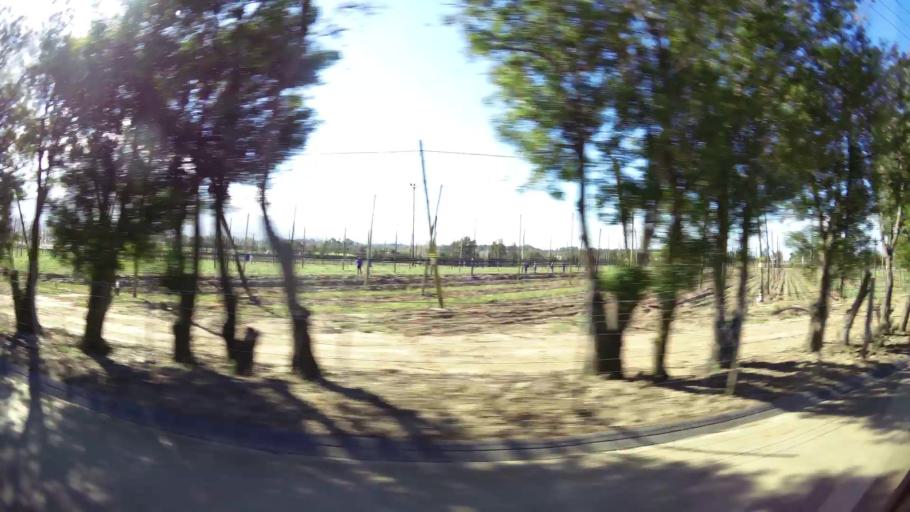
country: ZA
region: Western Cape
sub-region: Eden District Municipality
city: George
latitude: -33.9602
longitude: 22.3991
